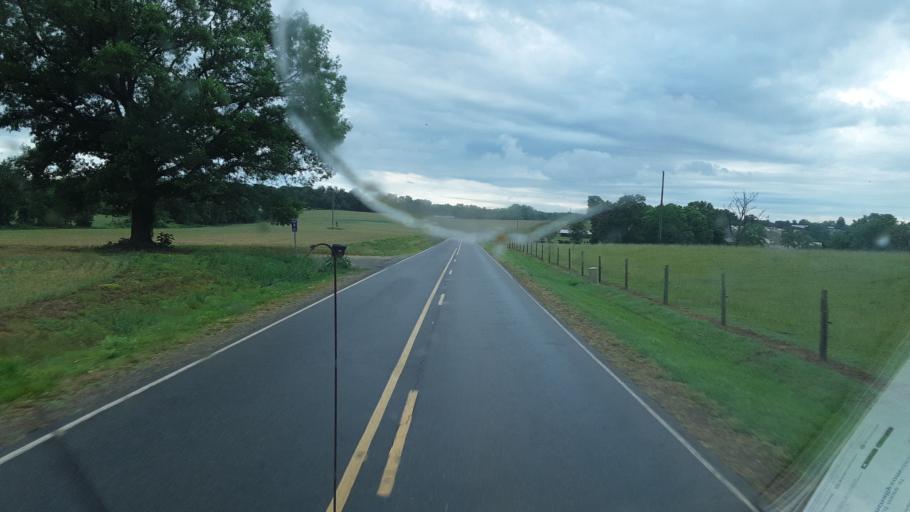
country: US
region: North Carolina
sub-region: Yadkin County
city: Jonesville
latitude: 36.0630
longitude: -80.8321
